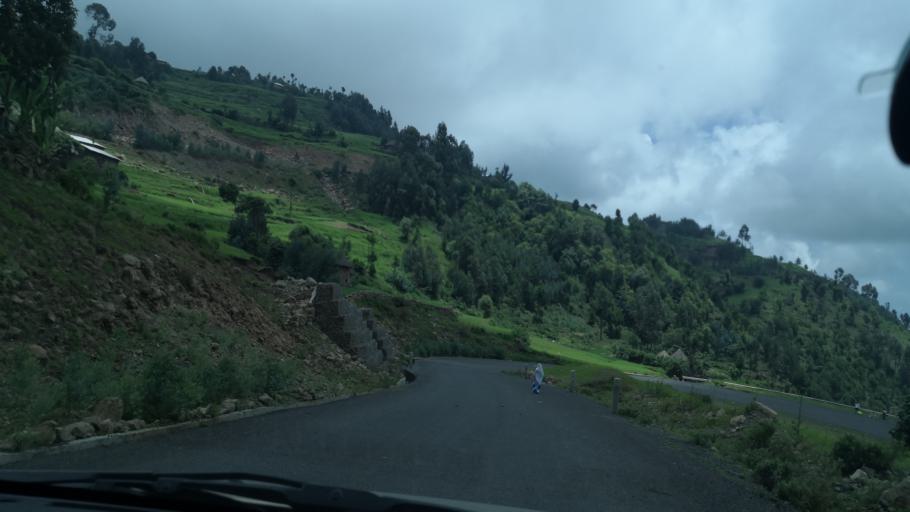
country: ET
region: Amhara
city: Abomsa
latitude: 10.3258
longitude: 39.8402
